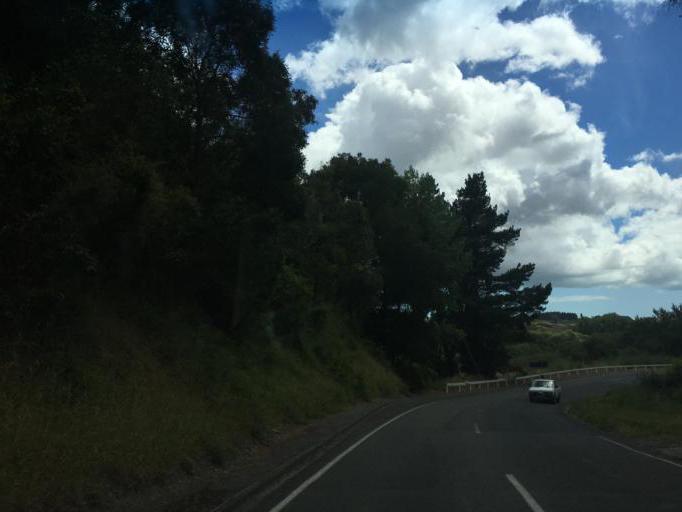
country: NZ
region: Hawke's Bay
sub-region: Hastings District
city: Hastings
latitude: -39.7356
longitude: 176.8990
